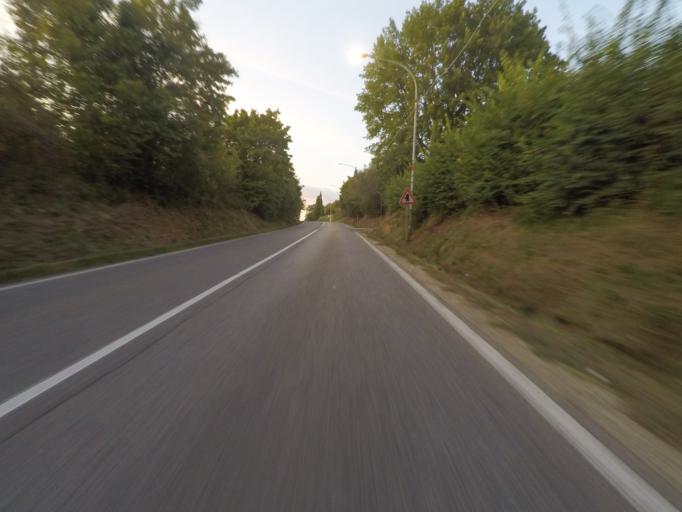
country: IT
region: Tuscany
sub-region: Provincia di Siena
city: Torrita di Siena
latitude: 43.1738
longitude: 11.7739
